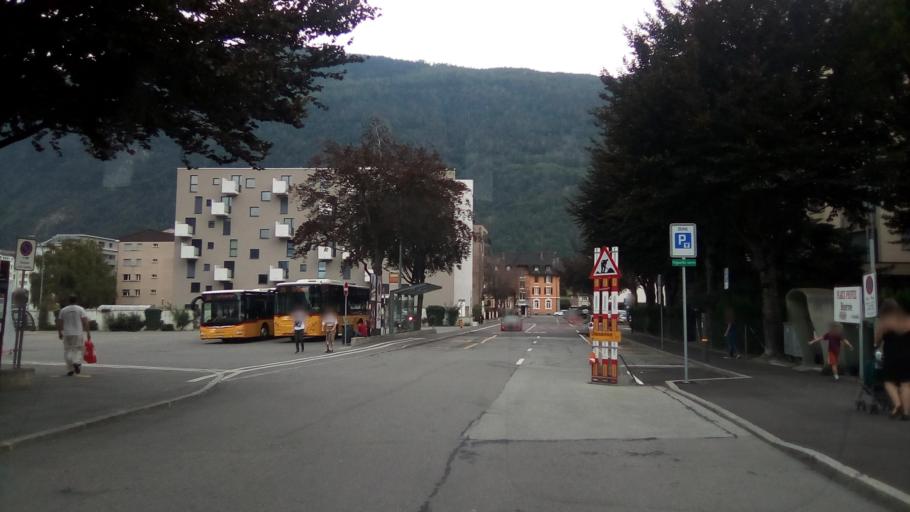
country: CH
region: Valais
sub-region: Martigny District
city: Martigny-Ville
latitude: 46.1055
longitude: 7.0794
